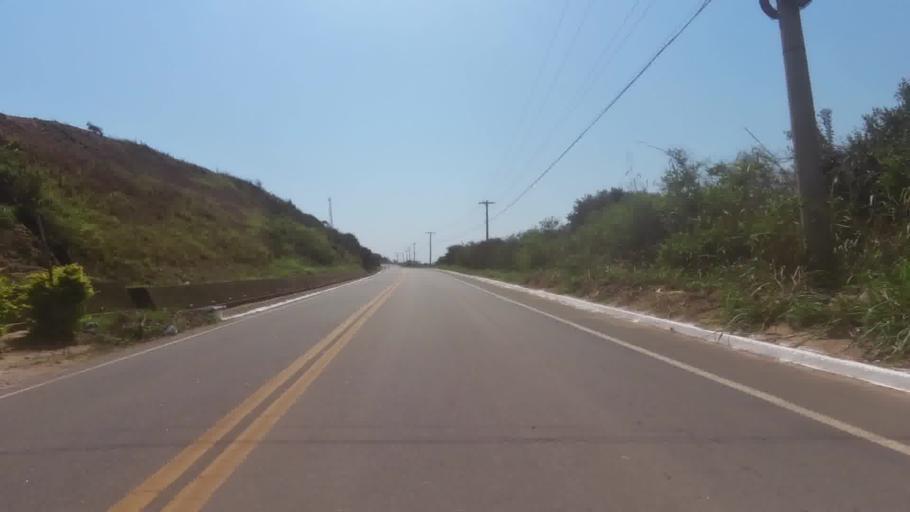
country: BR
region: Espirito Santo
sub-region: Marataizes
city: Marataizes
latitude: -21.0969
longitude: -40.8481
